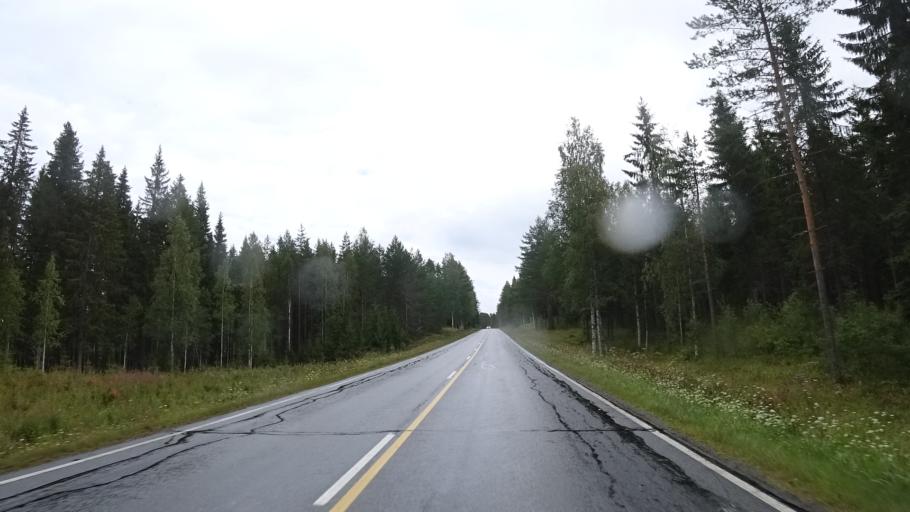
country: FI
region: North Karelia
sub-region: Keski-Karjala
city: Raeaekkylae
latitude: 62.0751
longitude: 29.6401
